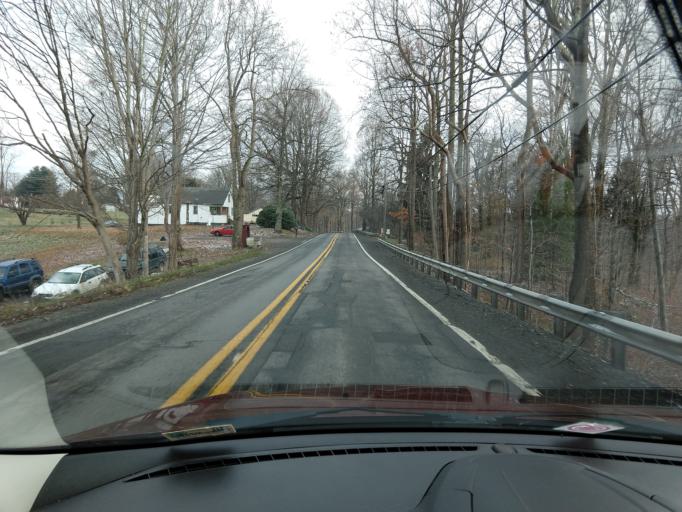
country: US
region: West Virginia
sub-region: Nicholas County
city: Craigsville
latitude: 38.2035
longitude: -80.6840
